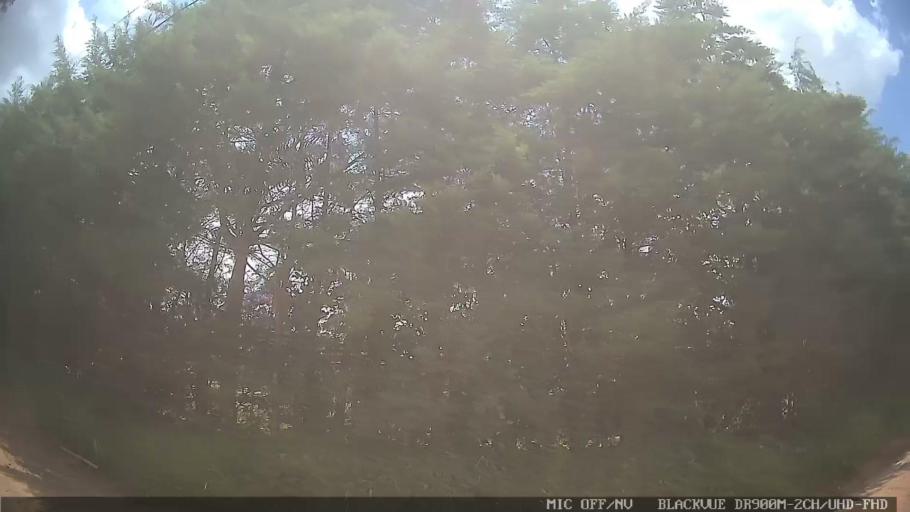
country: BR
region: Sao Paulo
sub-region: Atibaia
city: Atibaia
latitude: -23.0355
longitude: -46.5299
